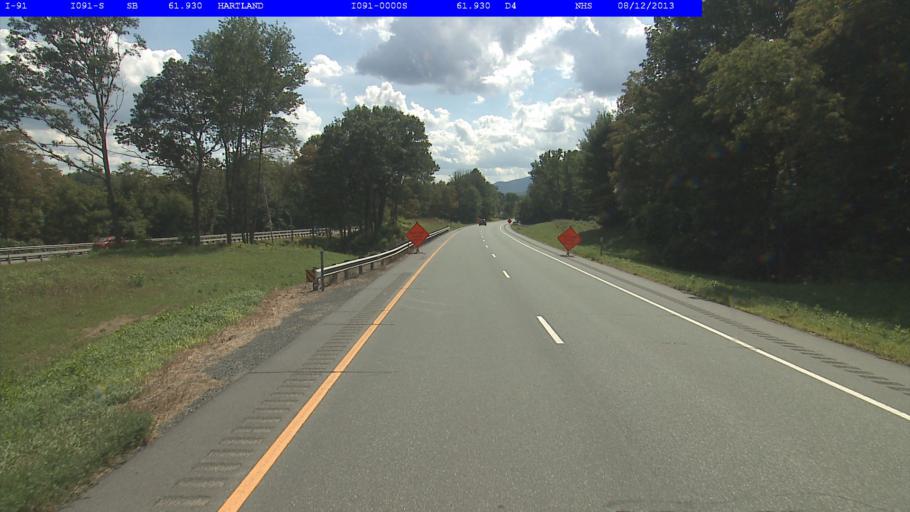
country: US
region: Vermont
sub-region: Windsor County
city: Windsor
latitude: 43.5453
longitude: -72.3863
